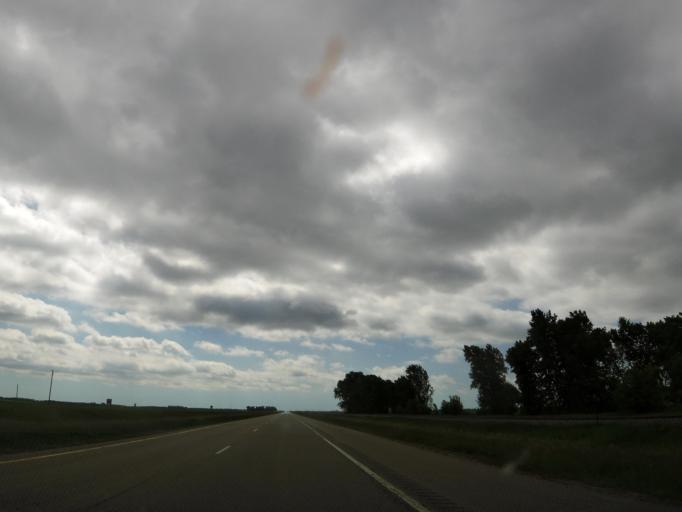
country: US
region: Minnesota
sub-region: Polk County
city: East Grand Forks
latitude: 47.8771
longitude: -96.9115
